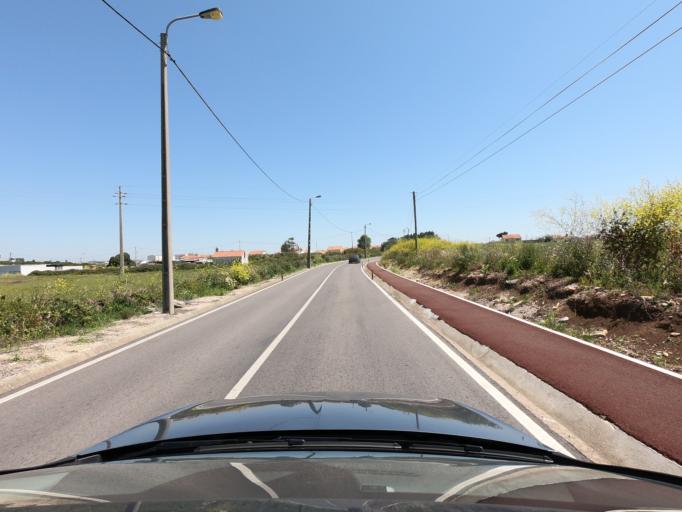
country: PT
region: Lisbon
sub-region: Cascais
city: Sao Domingos de Rana
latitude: 38.7332
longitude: -9.3472
